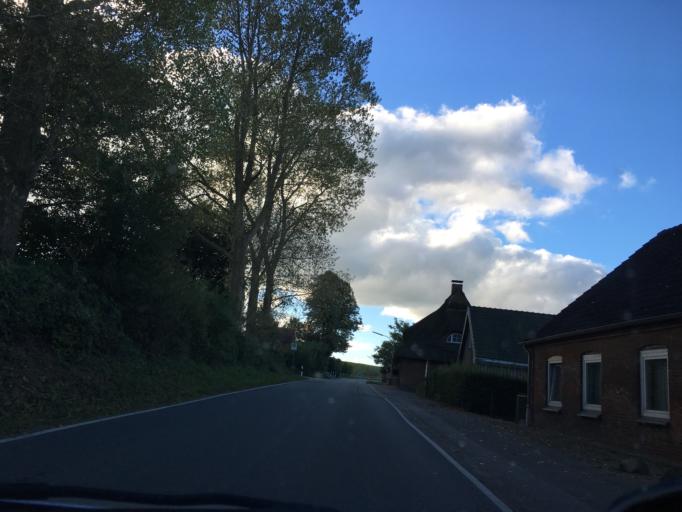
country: DE
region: Schleswig-Holstein
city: Achterwehr
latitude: 54.3190
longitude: 9.9743
